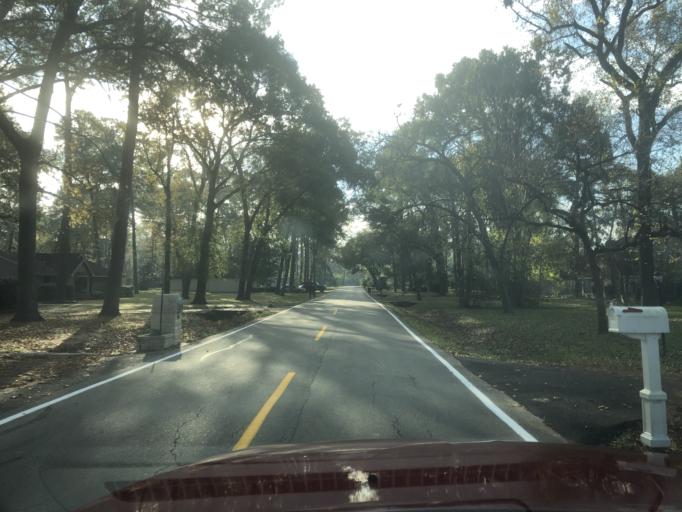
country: US
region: Texas
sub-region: Harris County
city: Spring
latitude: 30.0112
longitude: -95.4752
